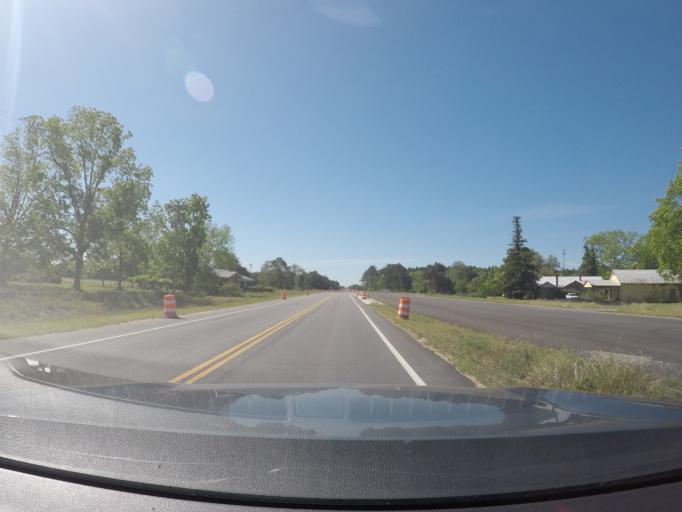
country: US
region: Georgia
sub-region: Bulloch County
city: Brooklet
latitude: 32.3452
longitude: -81.7399
